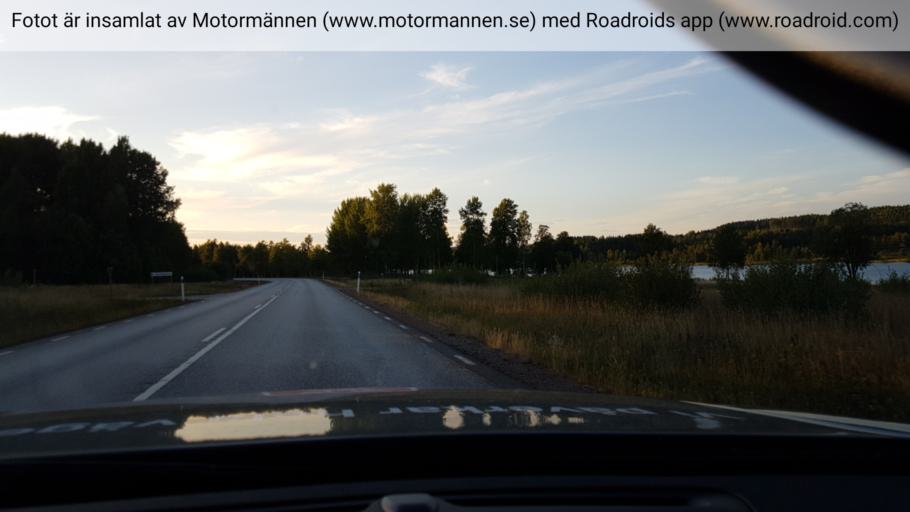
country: SE
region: Vaermland
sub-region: Storfors Kommun
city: Storfors
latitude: 59.5314
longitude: 14.2948
